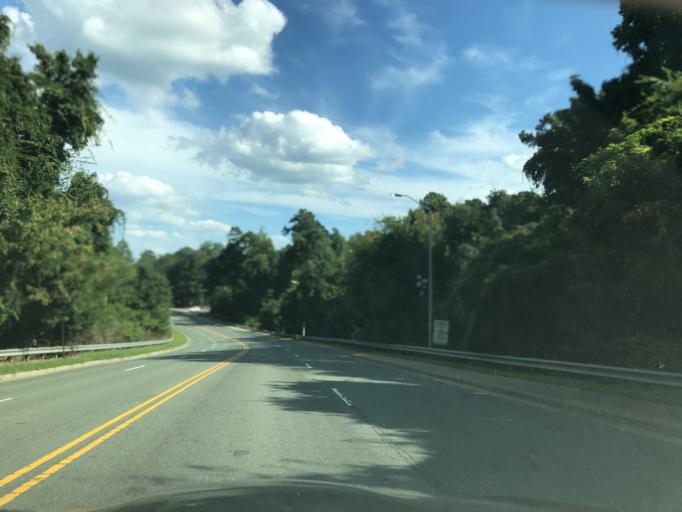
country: US
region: North Carolina
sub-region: Orange County
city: Chapel Hill
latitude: 35.9023
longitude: -79.0420
